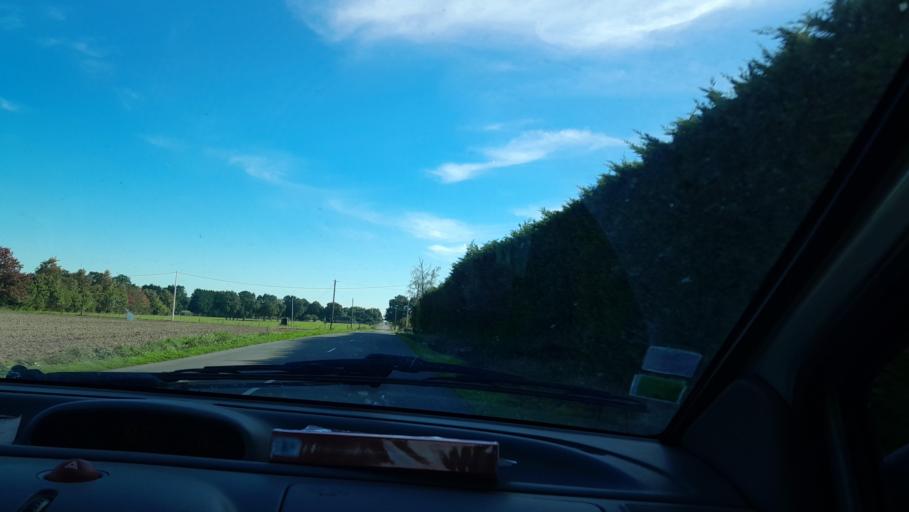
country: FR
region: Brittany
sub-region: Departement d'Ille-et-Vilaine
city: Argentre-du-Plessis
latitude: 48.0289
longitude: -1.1402
